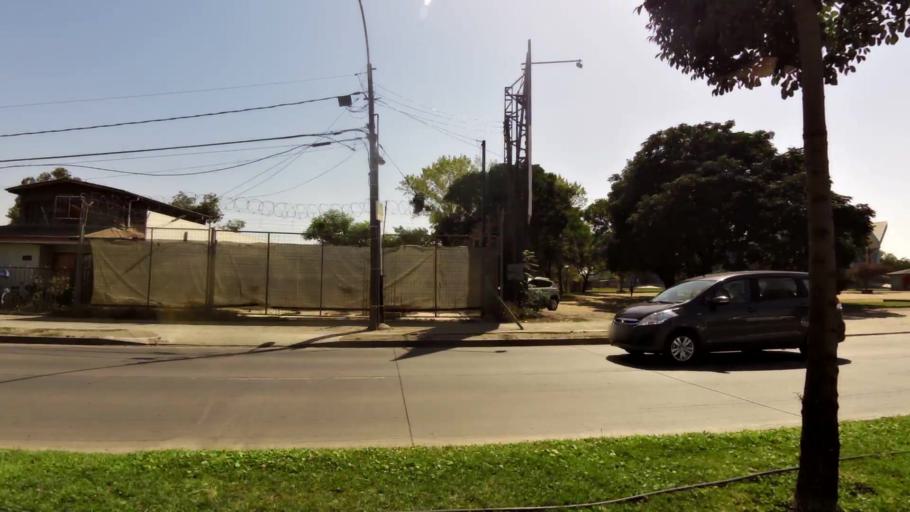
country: CL
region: Maule
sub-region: Provincia de Talca
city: Talca
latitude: -35.4272
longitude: -71.6415
